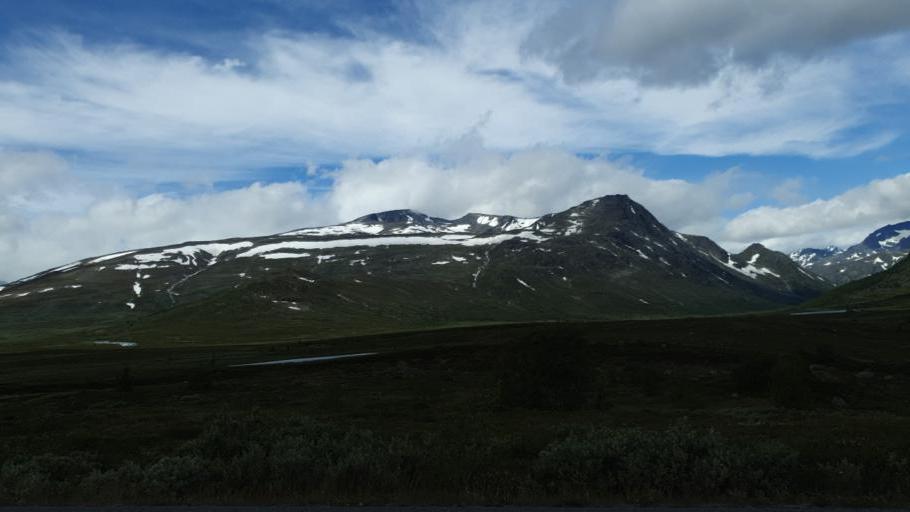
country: NO
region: Oppland
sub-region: Vang
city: Vang
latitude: 61.4606
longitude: 8.8063
